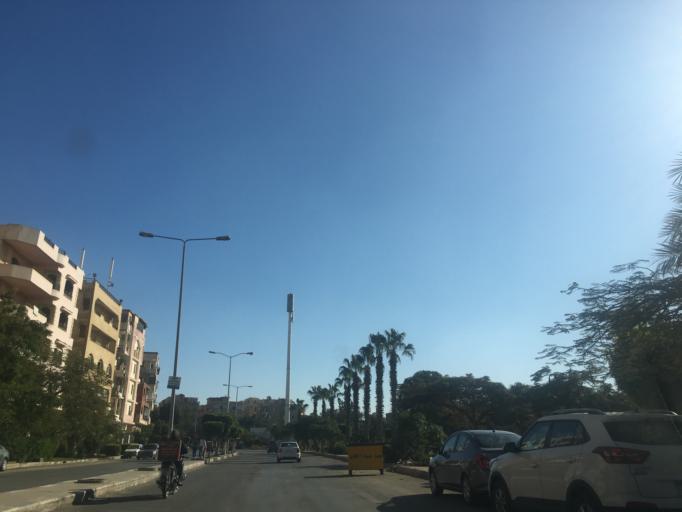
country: EG
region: Al Jizah
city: Madinat Sittah Uktubar
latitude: 29.9826
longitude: 30.9452
